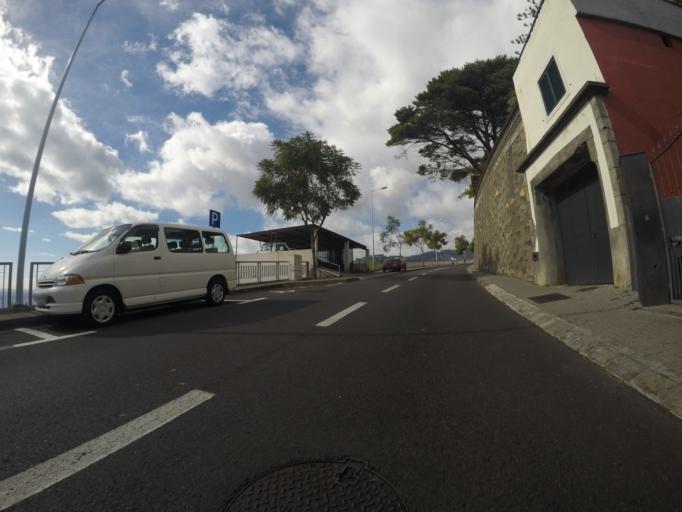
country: PT
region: Madeira
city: Camara de Lobos
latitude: 32.6455
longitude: -16.9584
